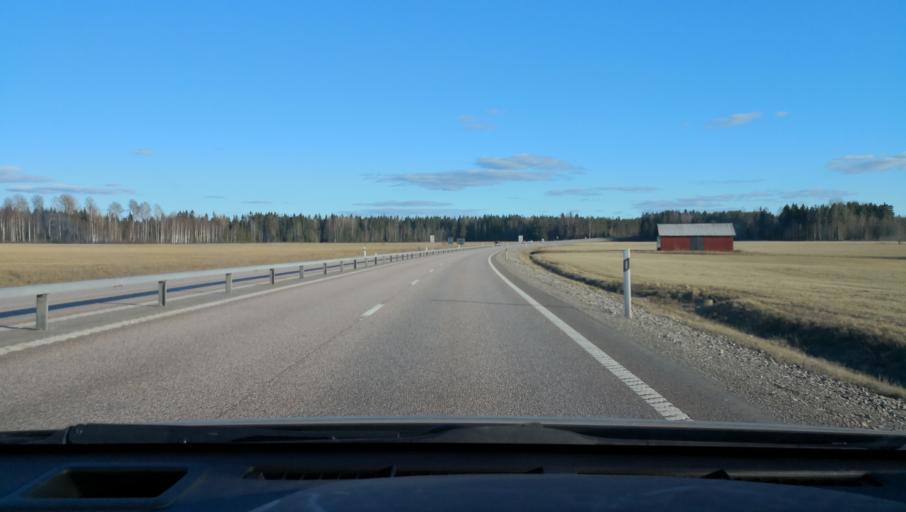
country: SE
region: Dalarna
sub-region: Avesta Kommun
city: Avesta
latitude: 60.0966
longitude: 16.3165
